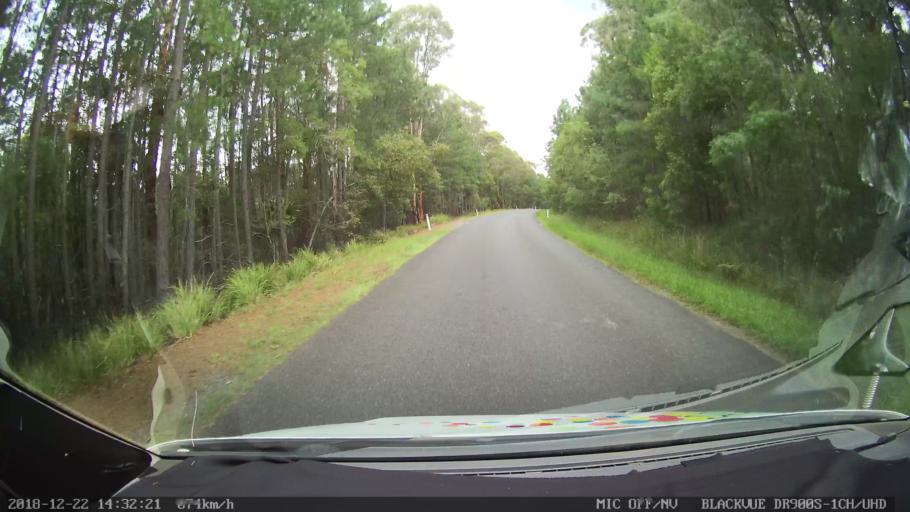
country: AU
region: New South Wales
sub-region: Bellingen
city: Dorrigo
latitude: -30.1030
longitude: 152.6267
